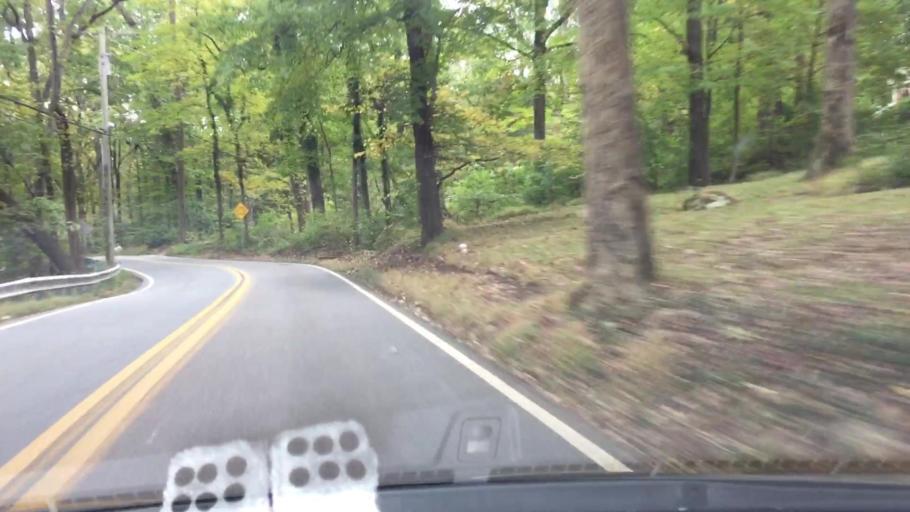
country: US
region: Pennsylvania
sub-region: Delaware County
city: Lima
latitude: 39.9276
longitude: -75.4235
